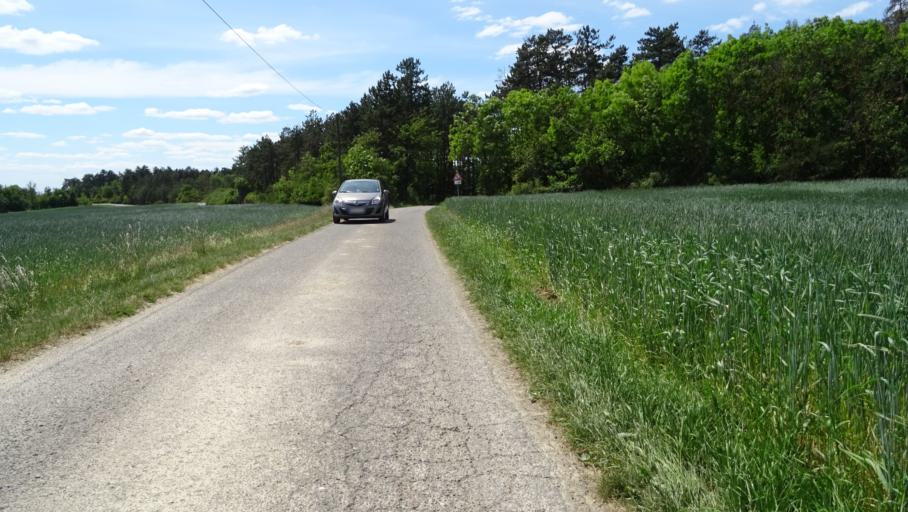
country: DE
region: Baden-Wuerttemberg
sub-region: Karlsruhe Region
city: Seckach
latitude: 49.4830
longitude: 9.3298
